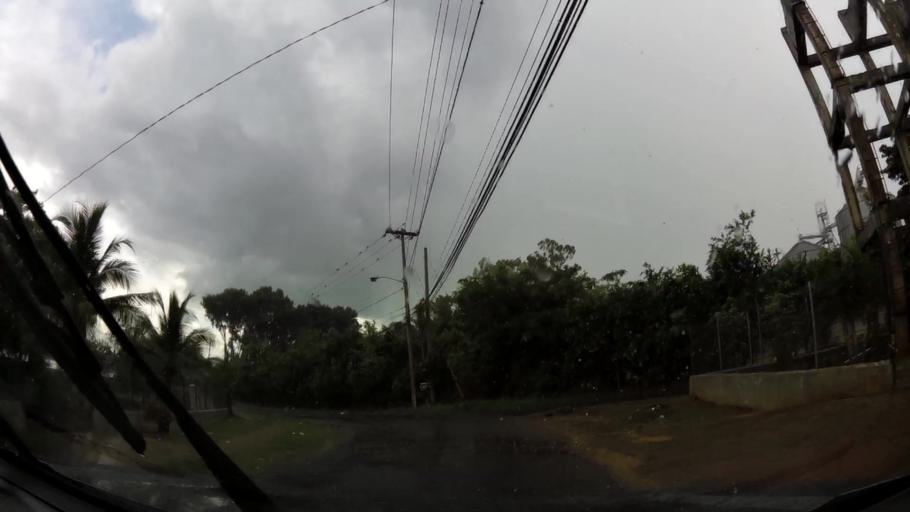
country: PA
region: Panama
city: Cabra Numero Uno
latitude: 9.1025
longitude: -79.3311
